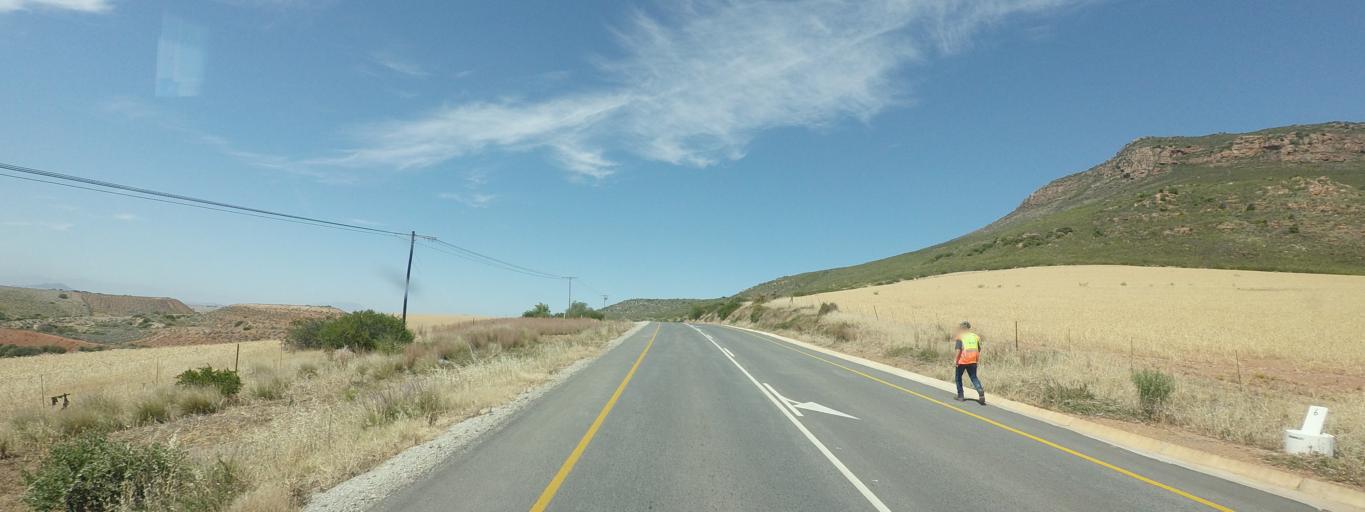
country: ZA
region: Western Cape
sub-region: West Coast District Municipality
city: Piketberg
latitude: -32.9232
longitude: 18.7570
